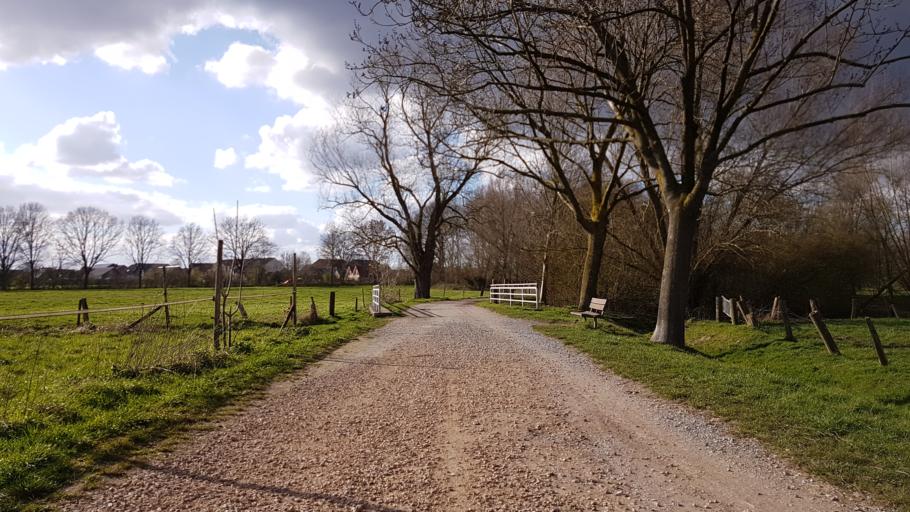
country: DE
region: North Rhine-Westphalia
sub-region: Regierungsbezirk Dusseldorf
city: Schwalmtal
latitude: 51.2246
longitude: 6.2513
